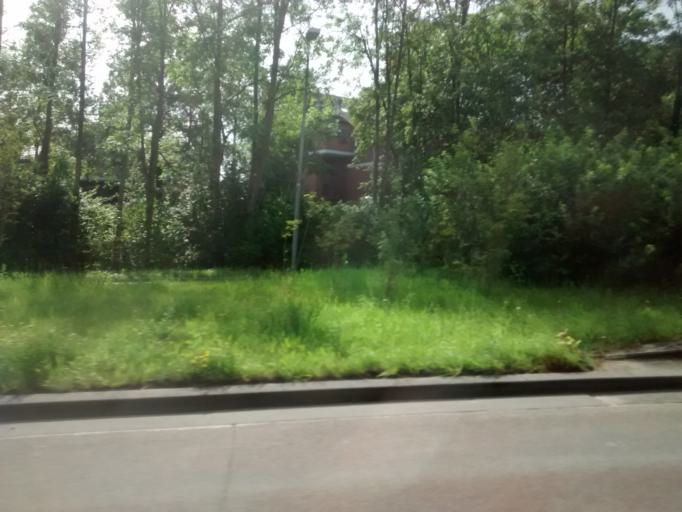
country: NL
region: Utrecht
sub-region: Gemeente De Bilt
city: De Bilt
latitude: 52.0892
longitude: 5.1551
